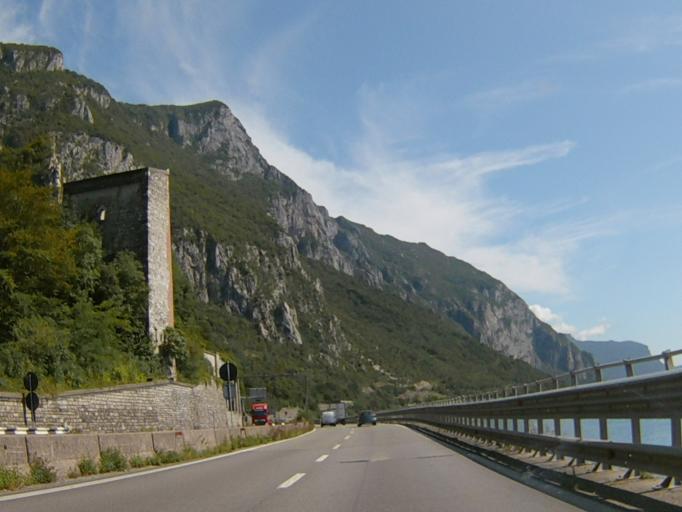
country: IT
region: Lombardy
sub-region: Provincia di Lecco
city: Abbadia Lariana
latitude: 45.8948
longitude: 9.3478
